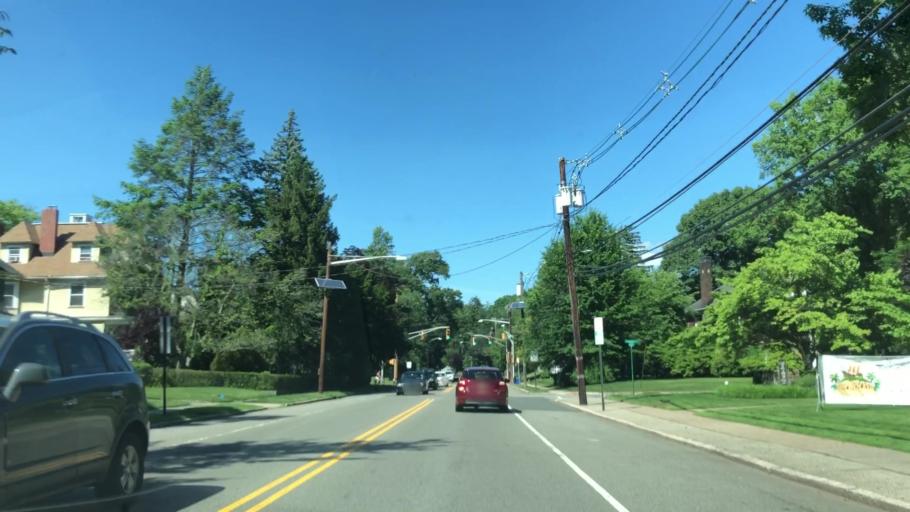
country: US
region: New Jersey
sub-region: Essex County
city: Montclair
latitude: 40.8177
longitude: -74.2054
